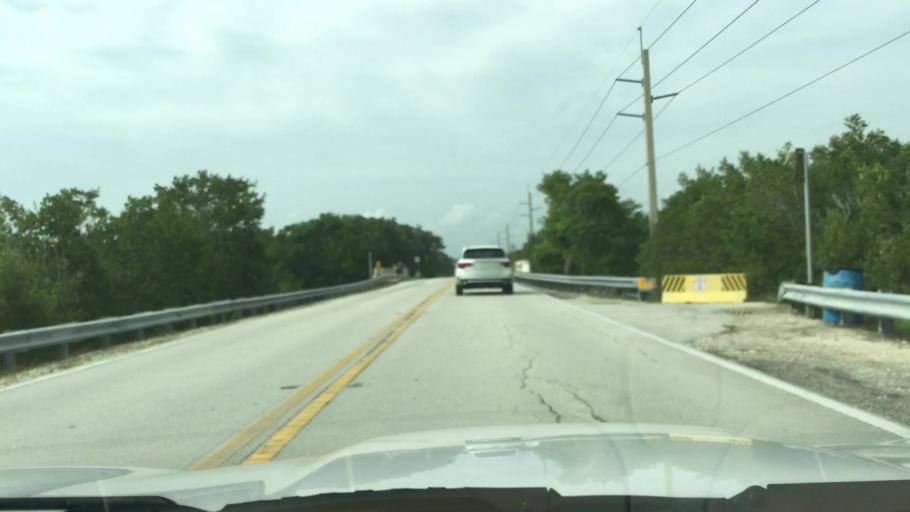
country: US
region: Florida
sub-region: Monroe County
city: North Key Largo
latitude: 25.2825
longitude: -80.3536
